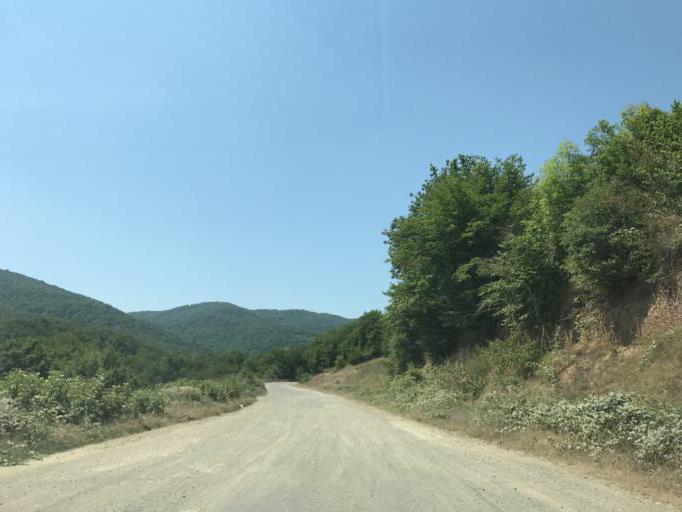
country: AZ
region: Tartar Rayon
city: Martakert
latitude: 40.1040
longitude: 46.6575
